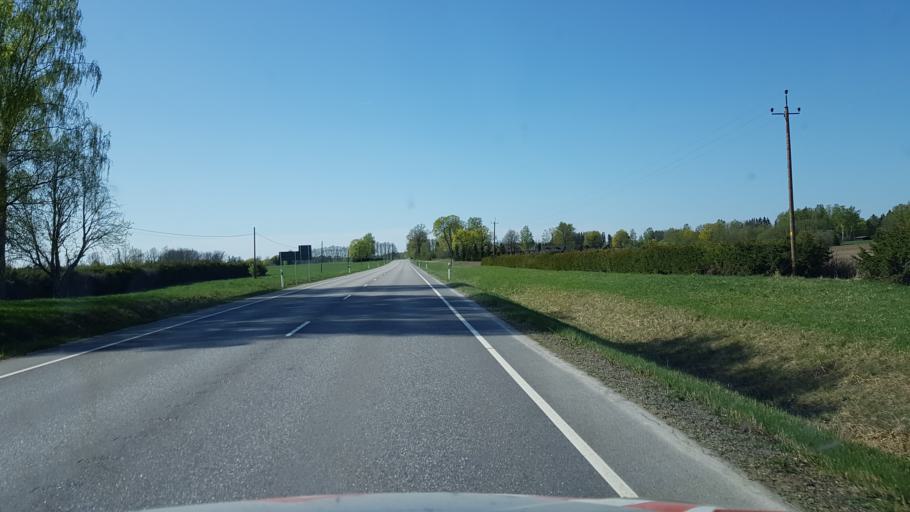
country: EE
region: Viljandimaa
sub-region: Karksi vald
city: Karksi-Nuia
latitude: 58.1112
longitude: 25.5094
